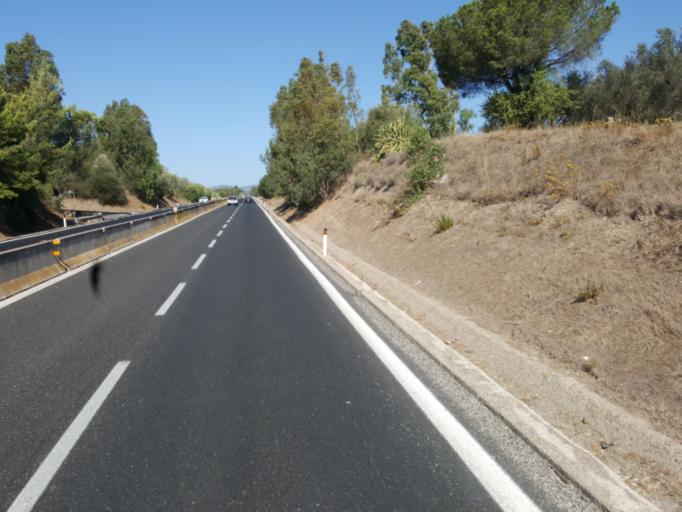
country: IT
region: Latium
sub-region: Provincia di Viterbo
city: Pescia Romana
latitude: 42.3986
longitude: 11.5130
